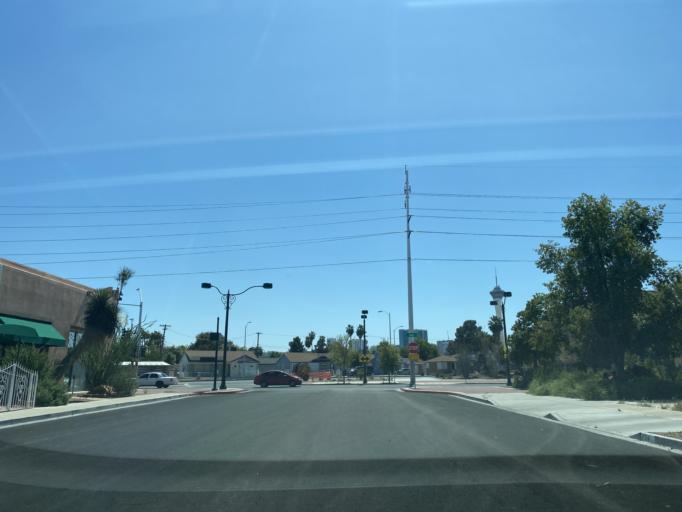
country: US
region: Nevada
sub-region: Clark County
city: Las Vegas
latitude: 36.1597
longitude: -115.1413
